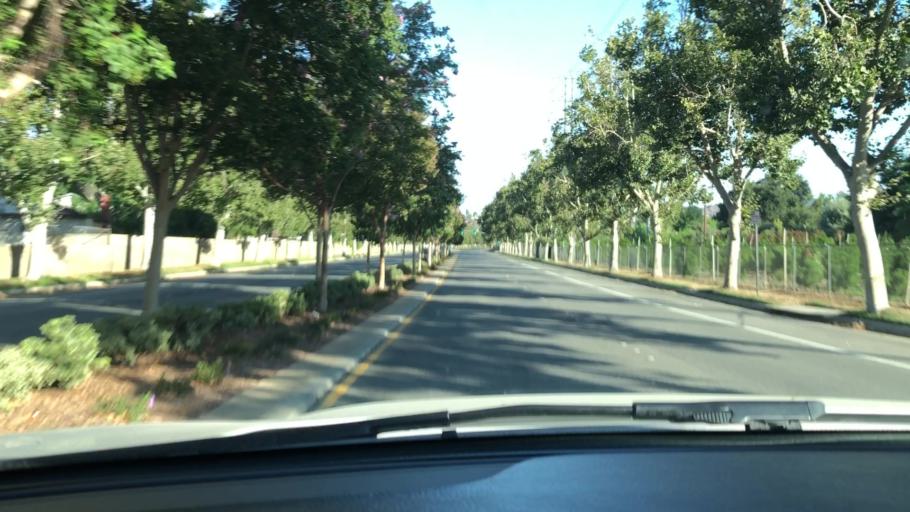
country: US
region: California
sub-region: Los Angeles County
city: Santa Clarita
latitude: 34.3870
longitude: -118.5453
